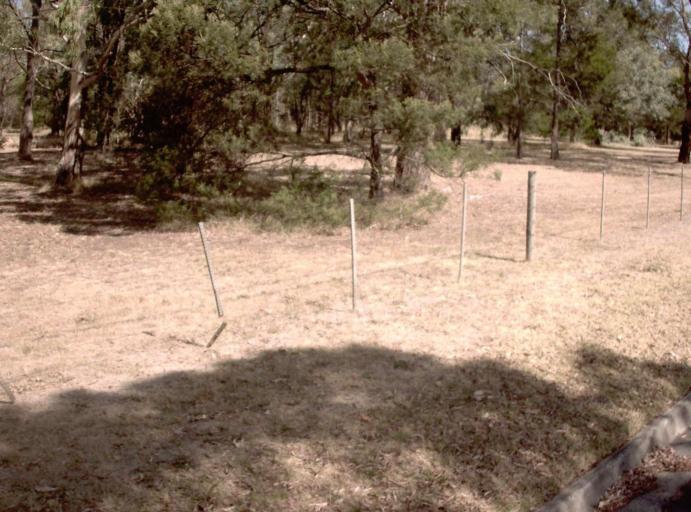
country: AU
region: Victoria
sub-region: Monash
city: Mulgrave
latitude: -37.8952
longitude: 145.1912
